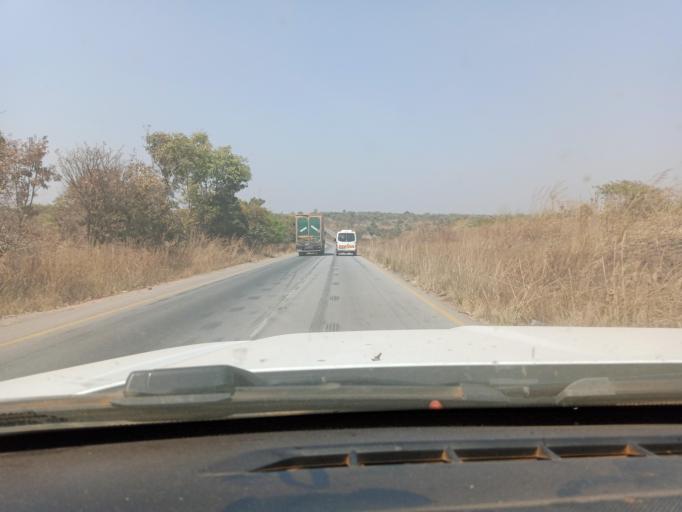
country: ZM
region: Copperbelt
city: Luanshya
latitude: -13.0139
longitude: 28.4342
